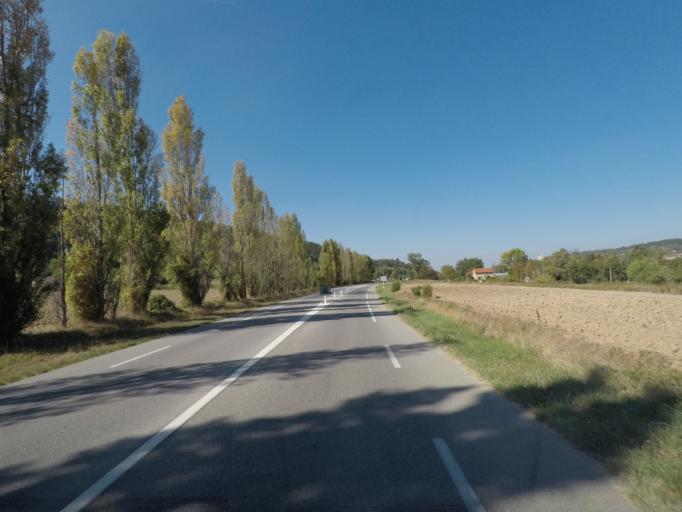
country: FR
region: Rhone-Alpes
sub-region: Departement de la Drome
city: Aouste-sur-Sye
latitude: 44.7152
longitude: 5.0436
